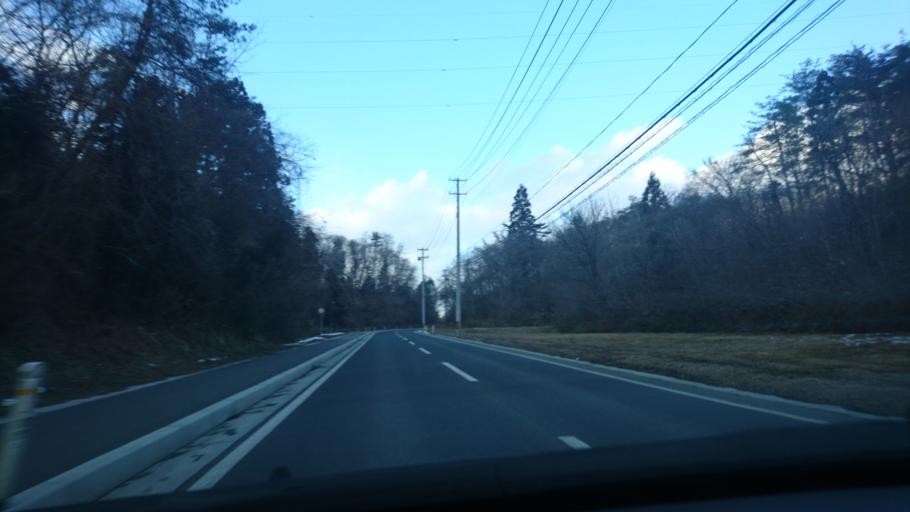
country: JP
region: Iwate
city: Ichinoseki
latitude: 39.0037
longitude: 141.3328
